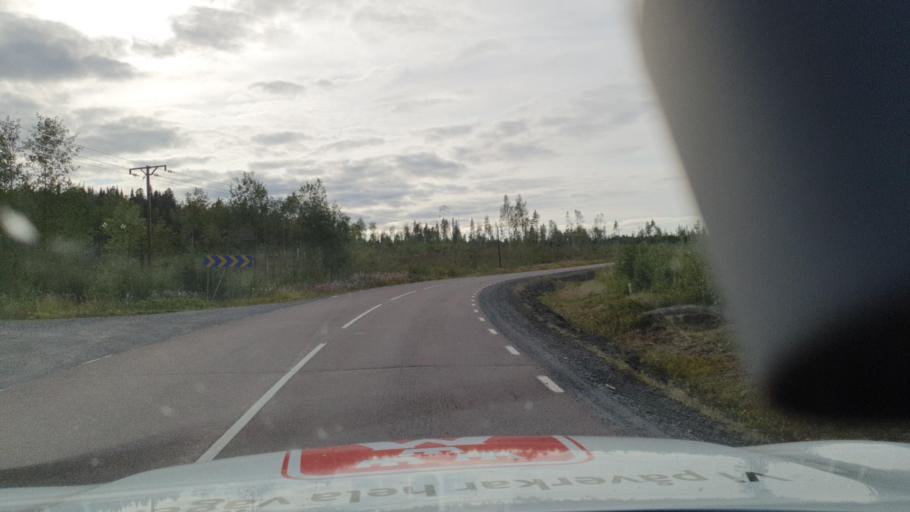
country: SE
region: Jaemtland
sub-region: Stroemsunds Kommun
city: Stroemsund
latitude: 63.8103
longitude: 15.6635
